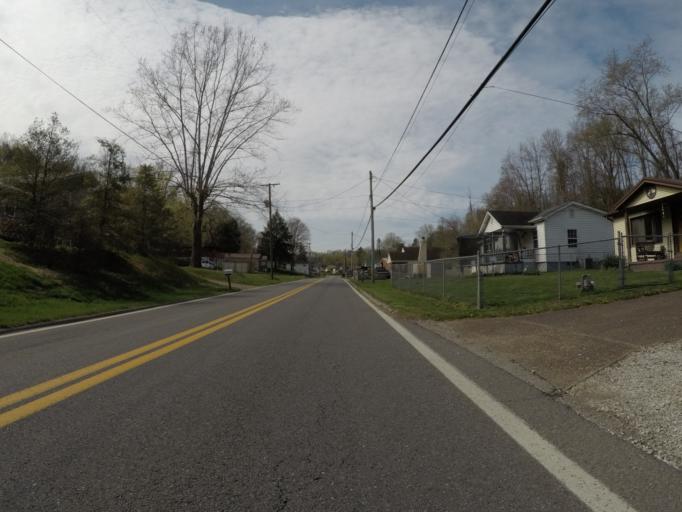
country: US
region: West Virginia
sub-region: Cabell County
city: Pea Ridge
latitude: 38.3706
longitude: -82.3712
